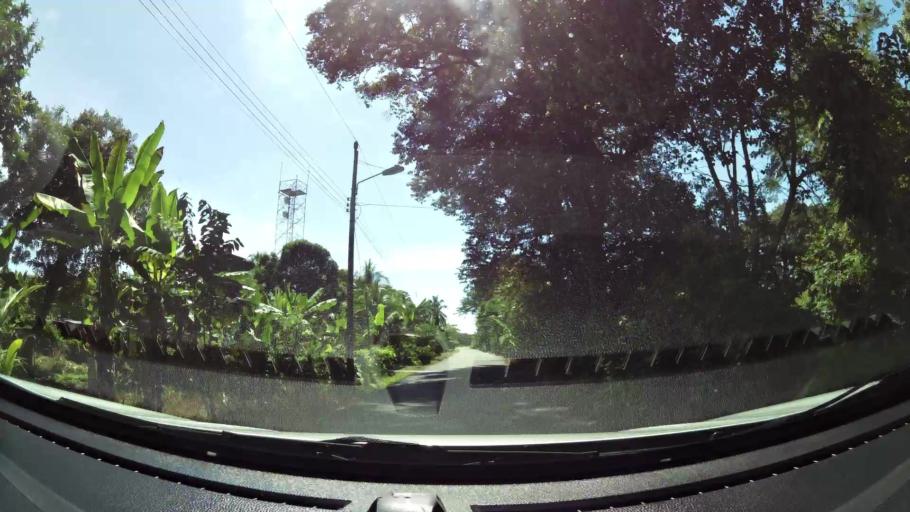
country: CR
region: Puntarenas
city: Quepos
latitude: 9.3299
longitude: -83.9570
